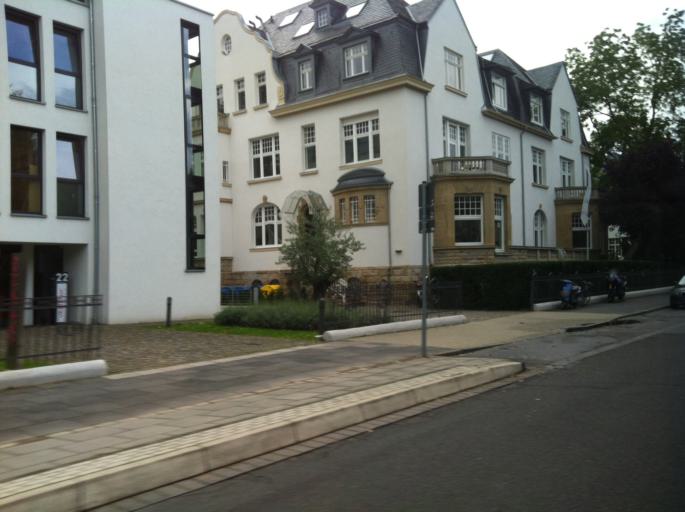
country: DE
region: North Rhine-Westphalia
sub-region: Regierungsbezirk Koln
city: Bonn
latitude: 50.7161
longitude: 7.1282
